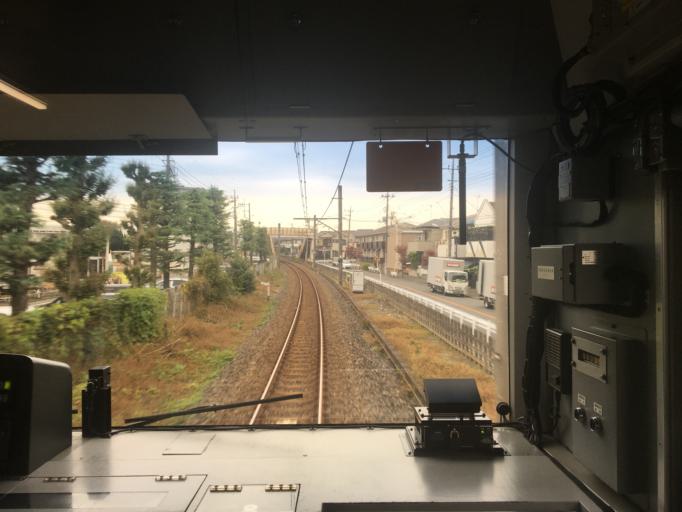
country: JP
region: Saitama
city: Kawagoe
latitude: 35.9211
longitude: 139.4488
